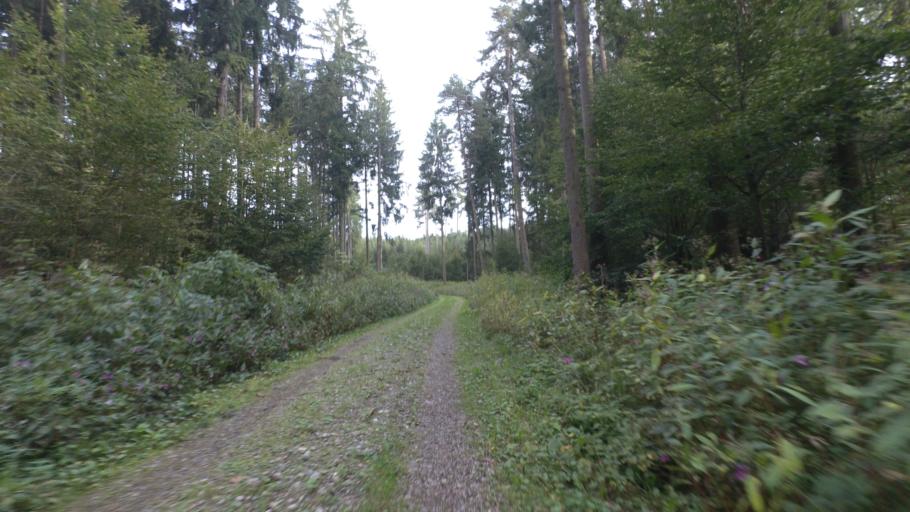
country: DE
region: Bavaria
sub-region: Upper Bavaria
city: Chieming
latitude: 47.9178
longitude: 12.5494
